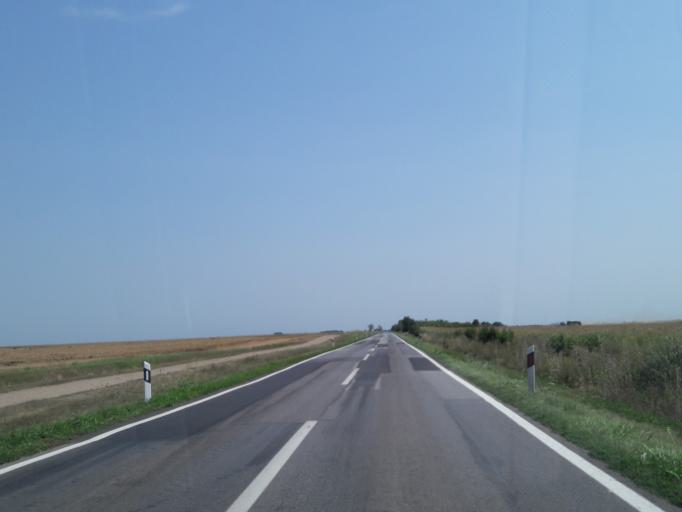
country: HR
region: Vukovarsko-Srijemska
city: Bobota
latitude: 45.4563
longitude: 18.8577
